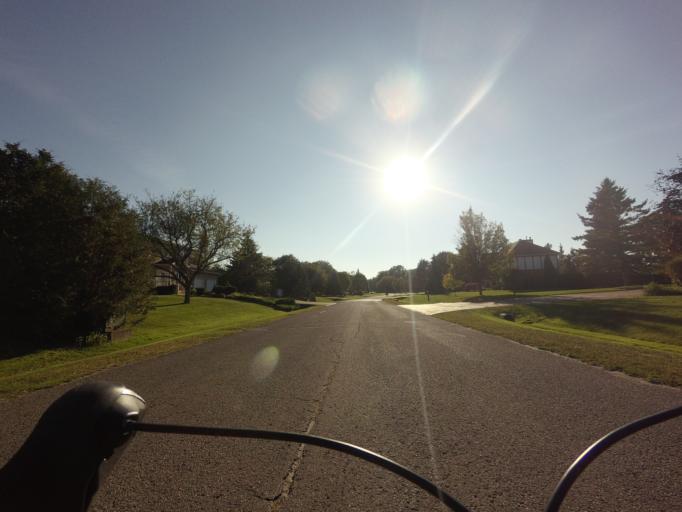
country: CA
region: Ontario
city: Bells Corners
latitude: 45.2203
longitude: -75.6863
